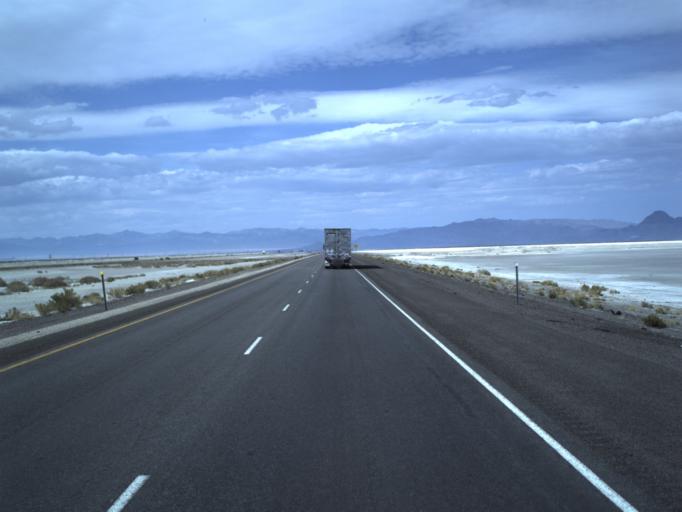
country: US
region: Utah
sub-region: Tooele County
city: Wendover
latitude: 40.7380
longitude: -113.7846
